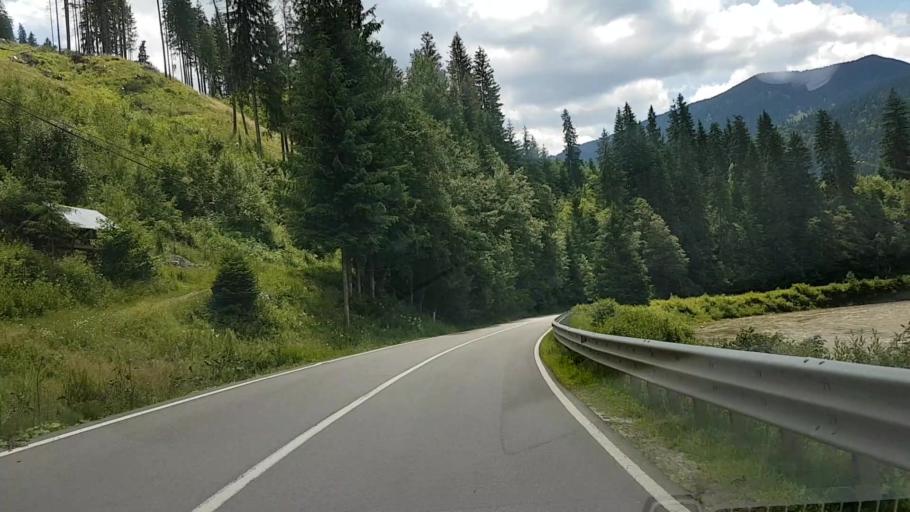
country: RO
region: Suceava
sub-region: Comuna Crucea
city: Crucea
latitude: 47.3538
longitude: 25.6157
